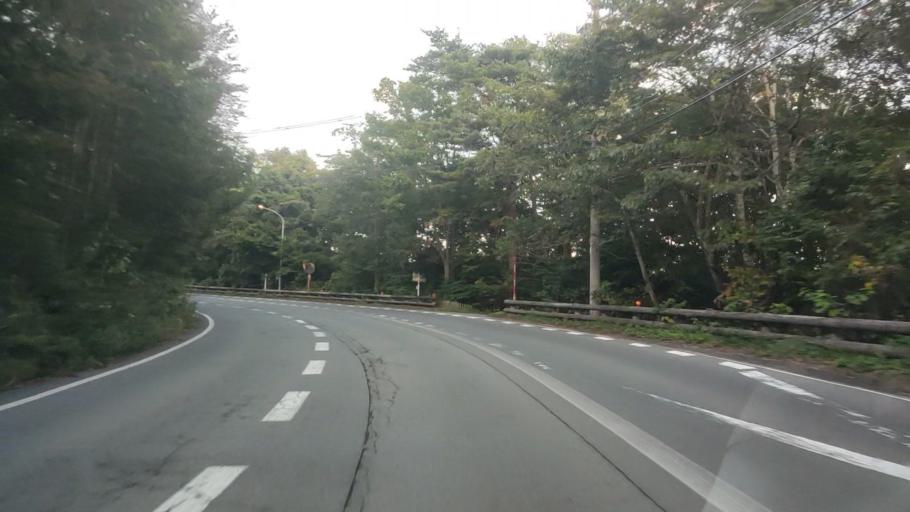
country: JP
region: Nagano
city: Komoro
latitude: 36.3846
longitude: 138.5902
